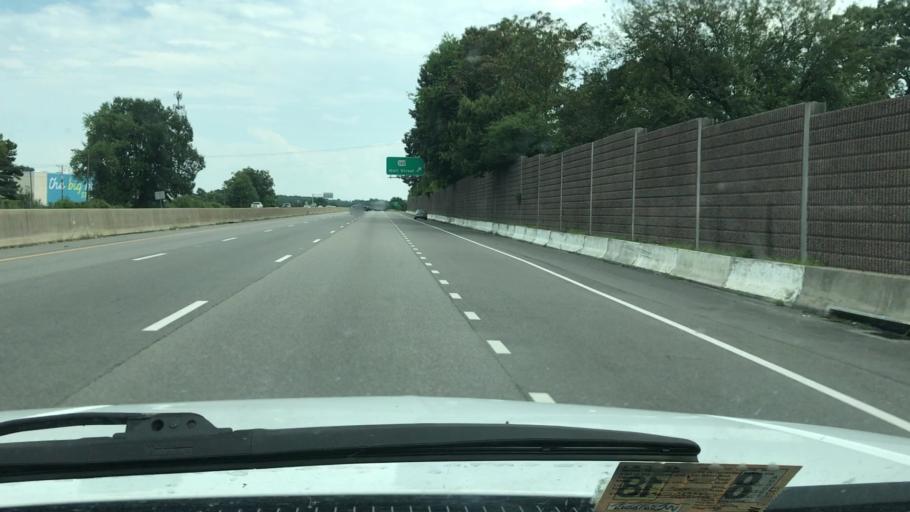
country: US
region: Virginia
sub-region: Chesterfield County
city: Bon Air
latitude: 37.4832
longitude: -77.5173
